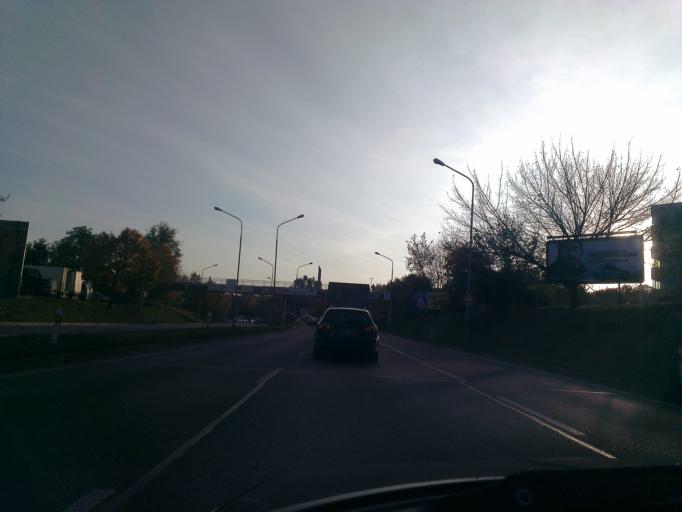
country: CZ
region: South Moravian
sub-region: Mesto Brno
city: Brno
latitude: 49.1715
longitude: 16.6005
